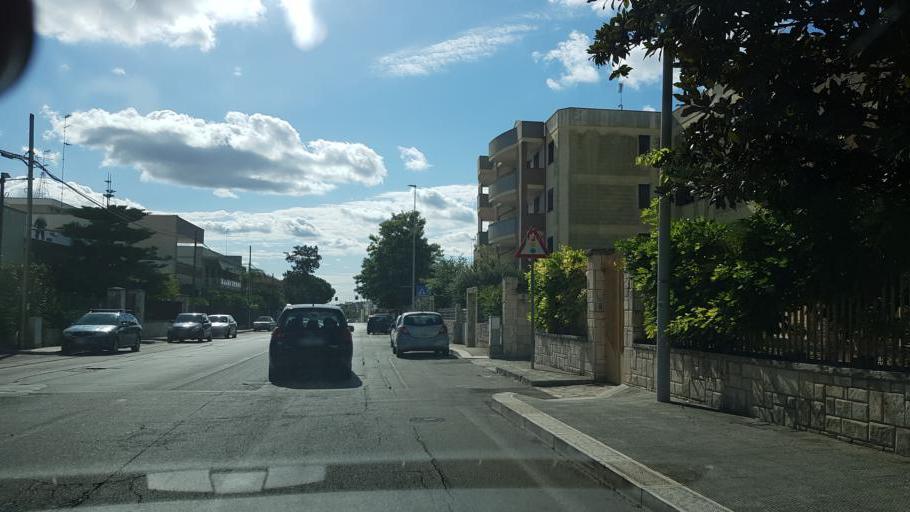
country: IT
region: Apulia
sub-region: Provincia di Lecce
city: Lecce
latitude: 40.3518
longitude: 18.1511
